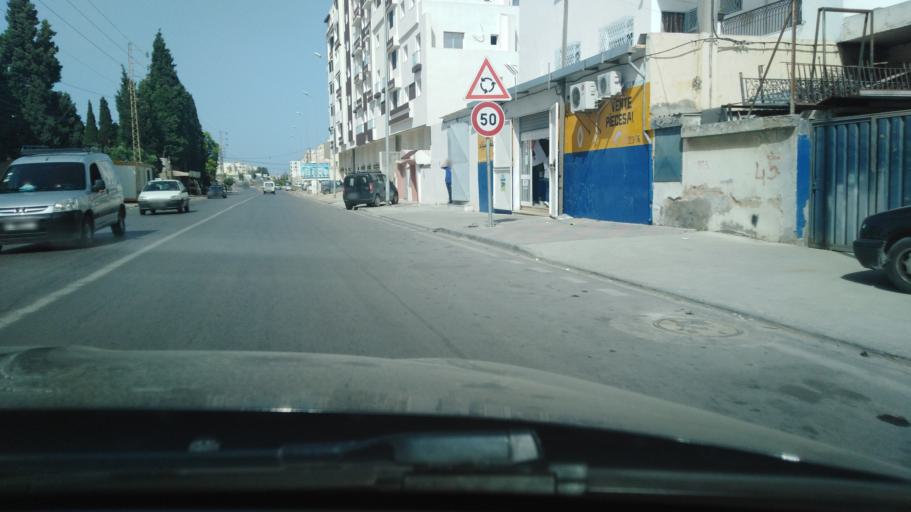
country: TN
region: Susah
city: Sousse
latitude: 35.8074
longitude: 10.6204
